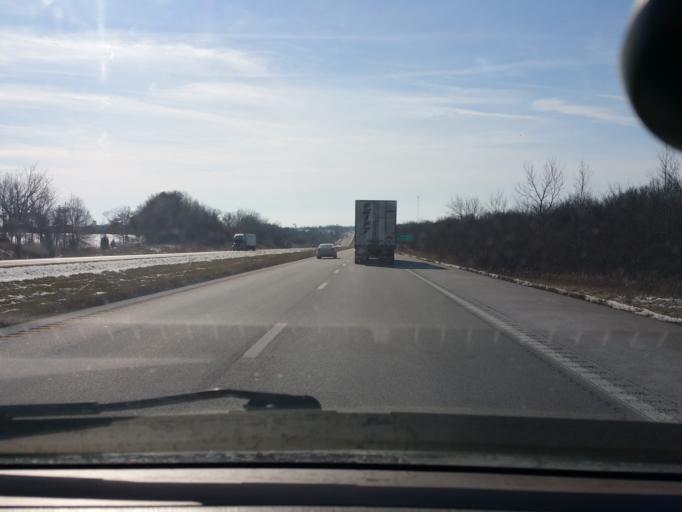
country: US
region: Missouri
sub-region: Clinton County
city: Cameron
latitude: 39.7786
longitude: -94.2102
